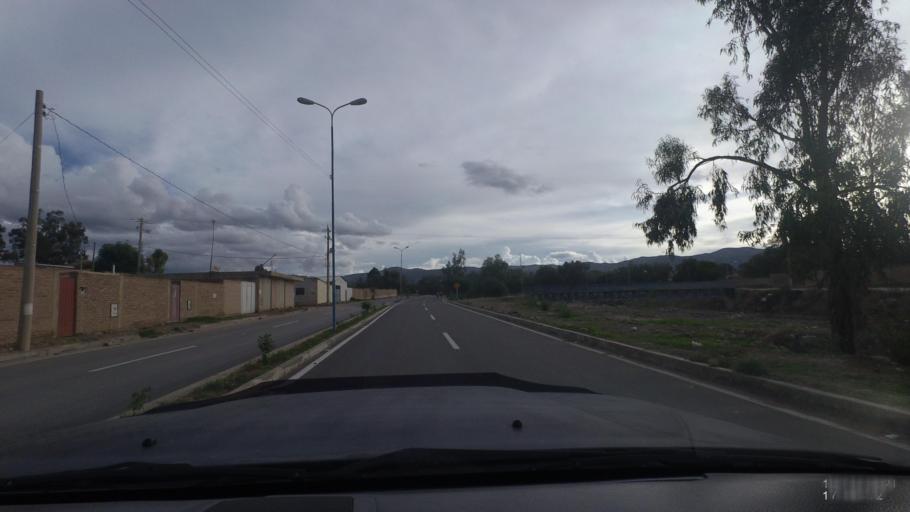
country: BO
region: Cochabamba
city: Tarata
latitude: -17.6125
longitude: -66.0208
